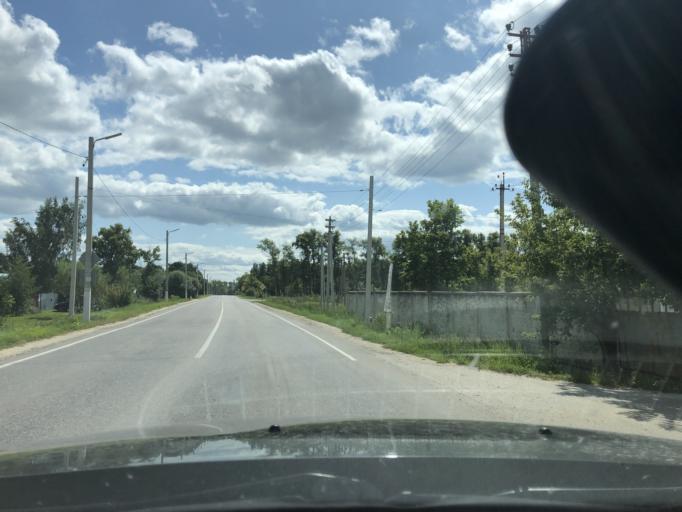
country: RU
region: Tula
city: Gorelki
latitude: 54.3403
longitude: 37.5632
